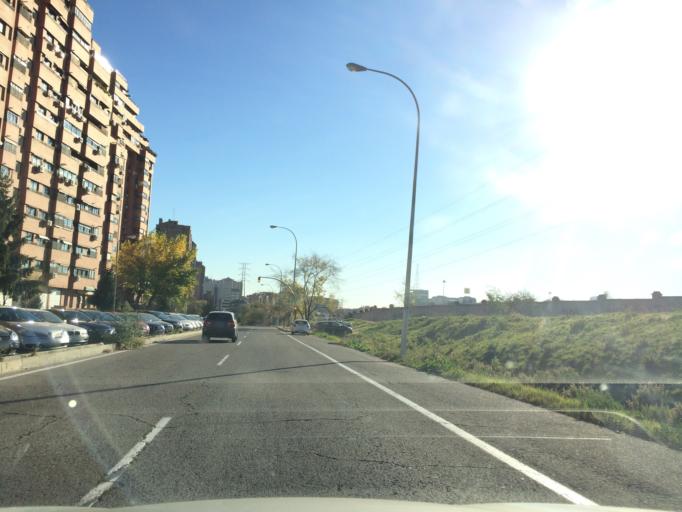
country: ES
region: Madrid
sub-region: Provincia de Madrid
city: Pinar de Chamartin
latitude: 40.4827
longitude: -3.6758
